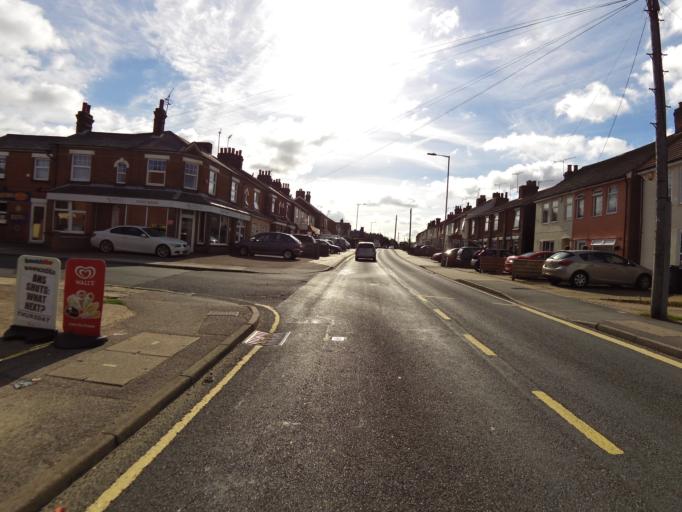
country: GB
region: England
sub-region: Suffolk
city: Bramford
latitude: 52.0676
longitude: 1.1246
